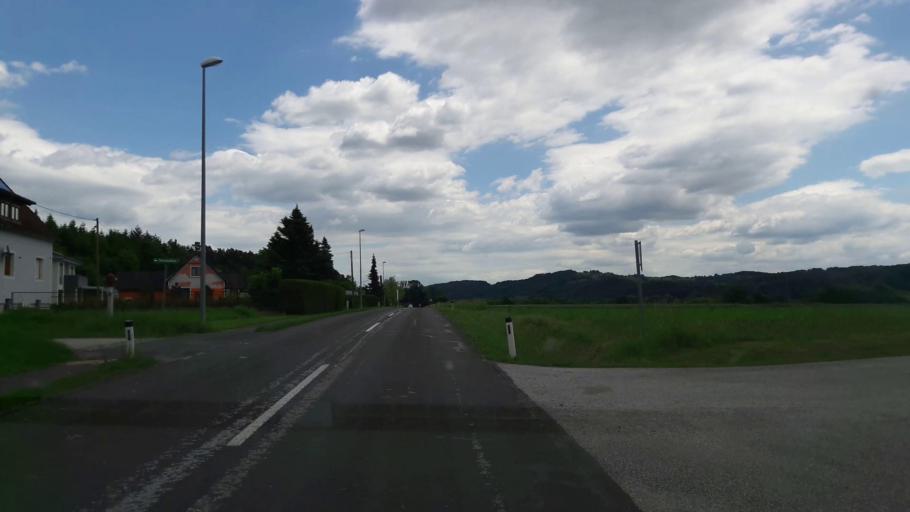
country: AT
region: Styria
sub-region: Politischer Bezirk Hartberg-Fuerstenfeld
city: Soechau
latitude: 47.0297
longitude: 16.0255
